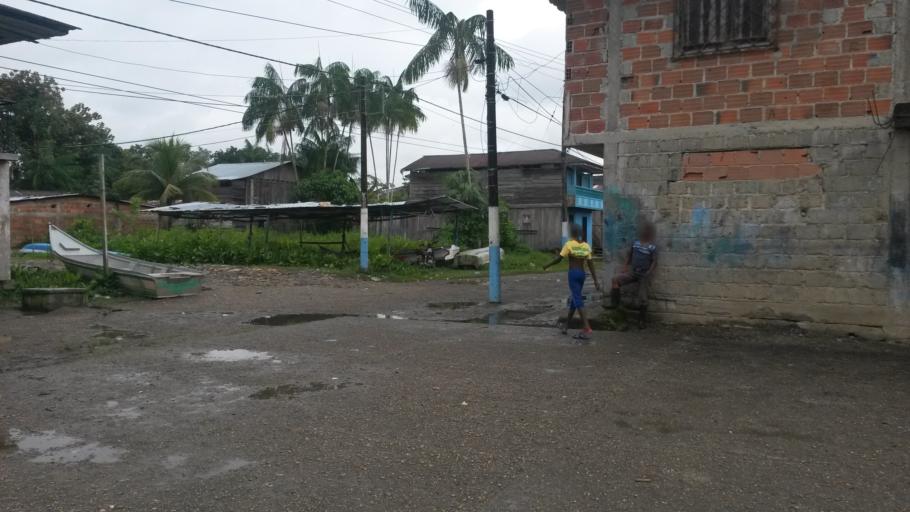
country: CO
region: Cauca
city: Guapi
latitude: 2.5675
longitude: -77.8830
